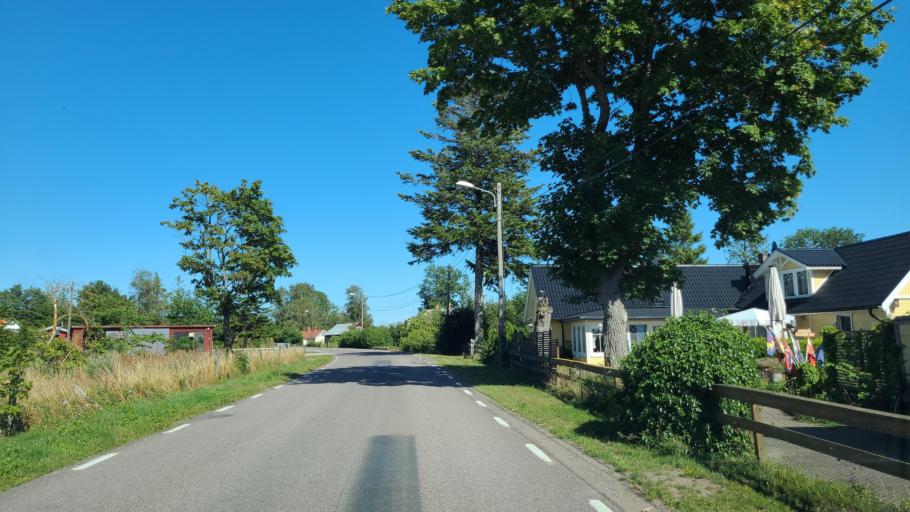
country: SE
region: Kalmar
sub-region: Borgholms Kommun
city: Borgholm
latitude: 56.8417
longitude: 16.7902
